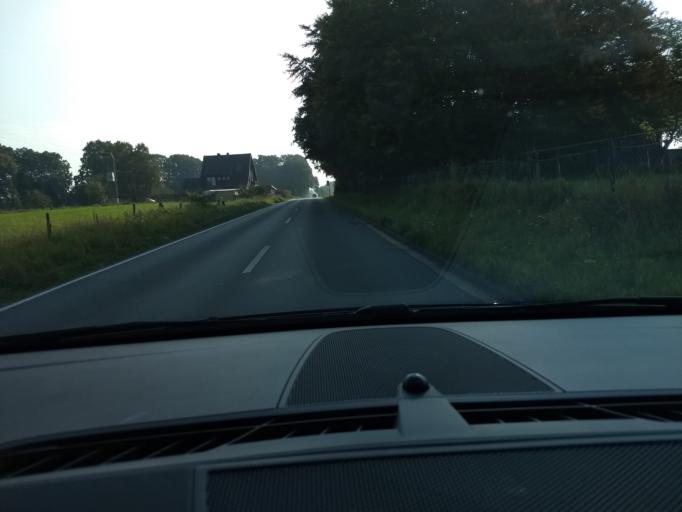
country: DE
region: North Rhine-Westphalia
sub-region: Regierungsbezirk Munster
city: Heiden
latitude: 51.8103
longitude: 6.9740
